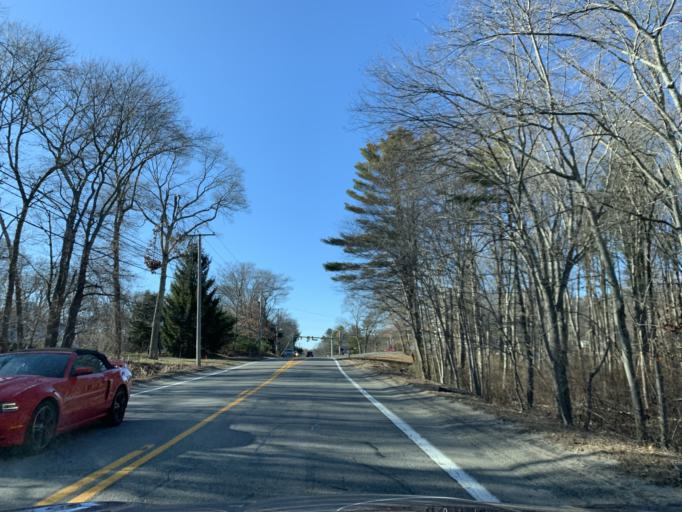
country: US
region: Rhode Island
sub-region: Providence County
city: North Providence
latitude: 41.8880
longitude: -71.4869
